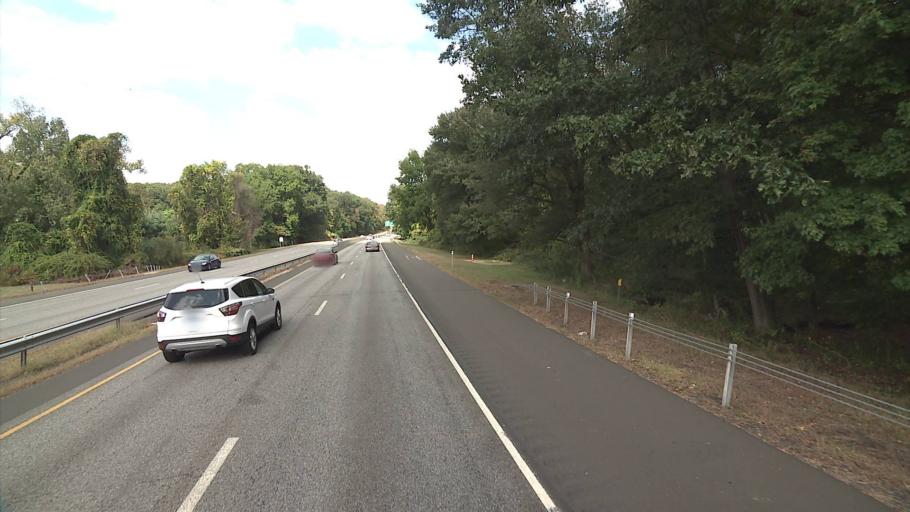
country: US
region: Connecticut
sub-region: New Haven County
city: Wallingford
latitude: 41.4525
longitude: -72.8405
